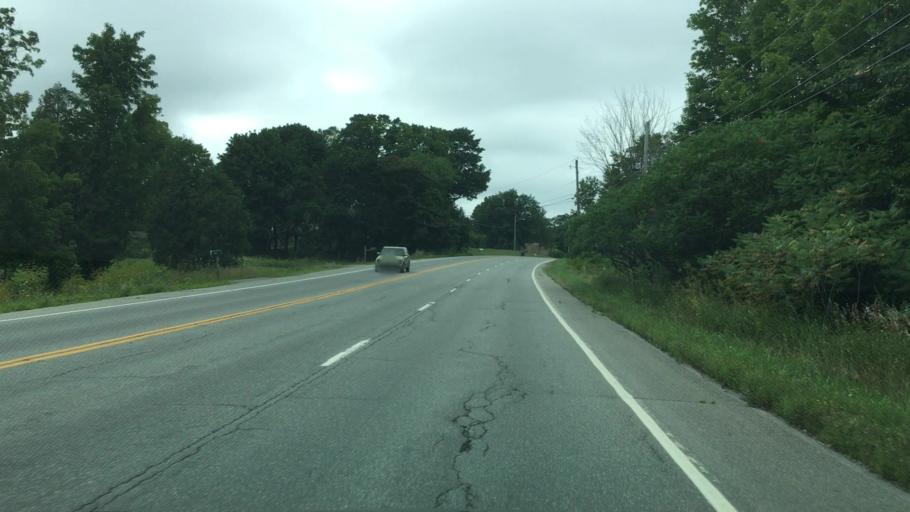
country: US
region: Maine
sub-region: Penobscot County
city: Orrington
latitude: 44.7059
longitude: -68.8459
